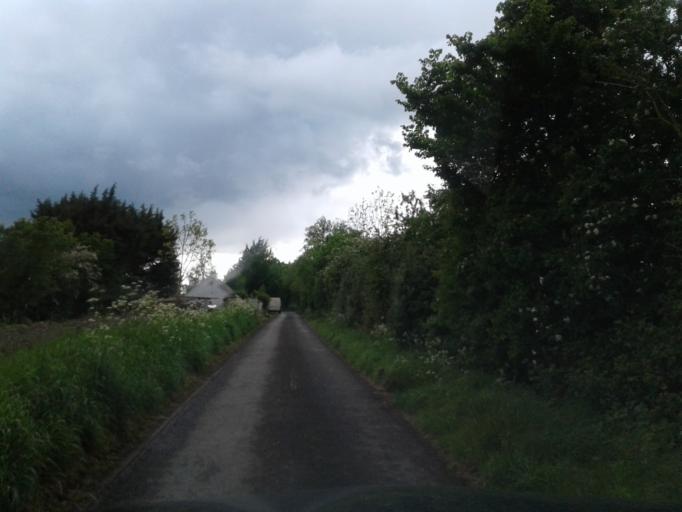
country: IE
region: Leinster
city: Ballymun
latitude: 53.4260
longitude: -6.2761
